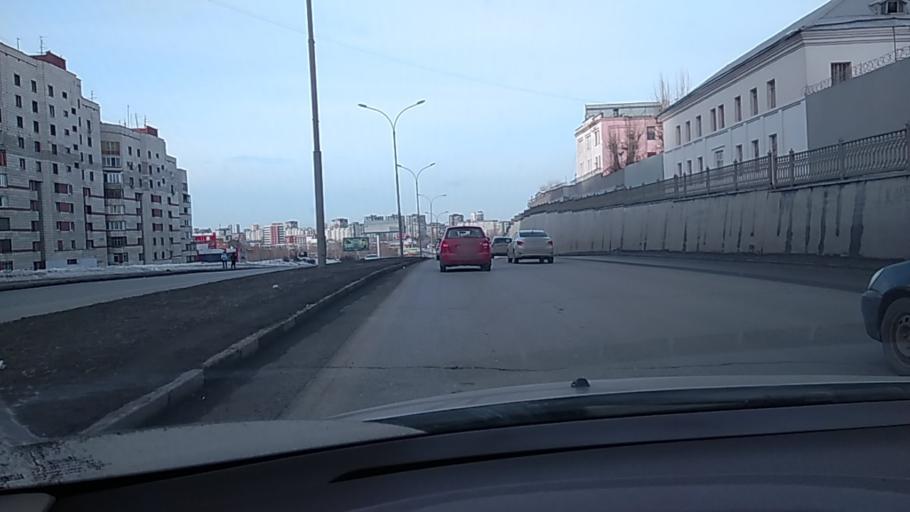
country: RU
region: Sverdlovsk
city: Yekaterinburg
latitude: 56.8368
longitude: 60.5622
